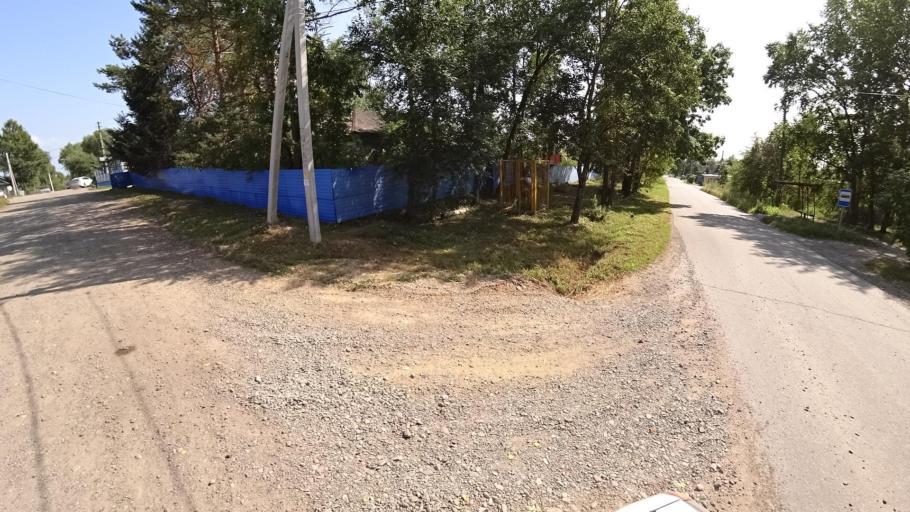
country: RU
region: Khabarovsk Krai
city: Khor
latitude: 47.9626
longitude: 135.0561
